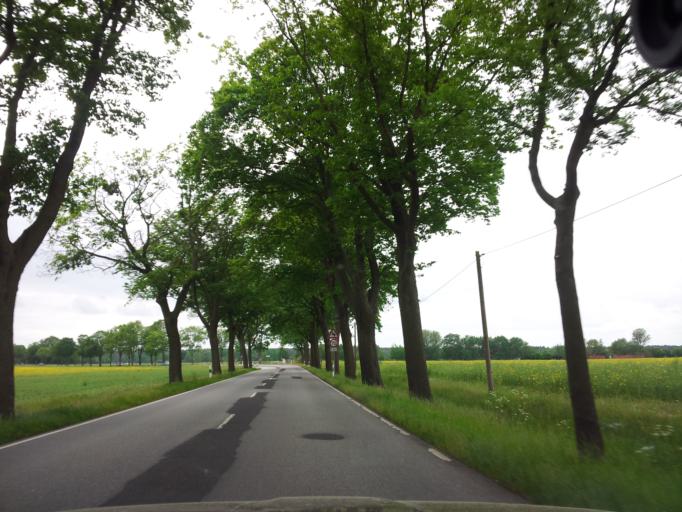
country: DE
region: Brandenburg
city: Brieselang
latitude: 52.6354
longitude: 13.0327
